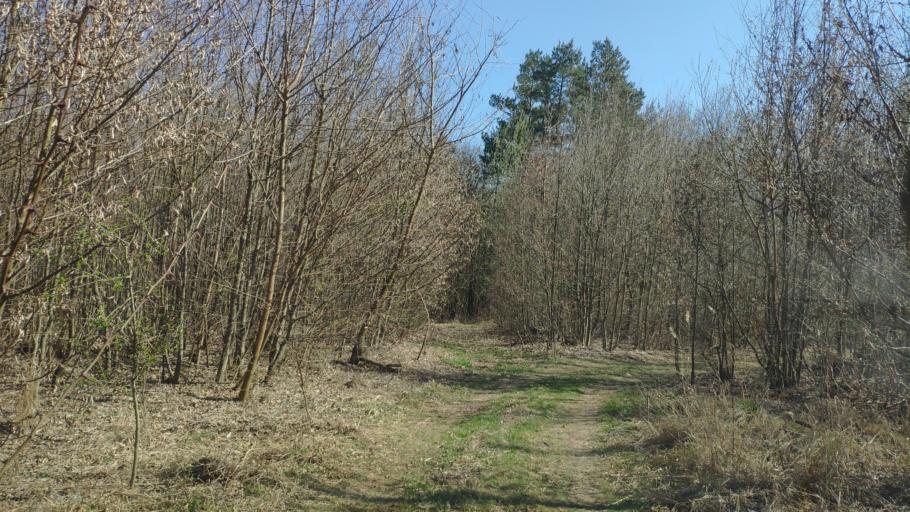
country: SK
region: Kosicky
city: Moldava nad Bodvou
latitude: 48.5611
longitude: 20.9329
